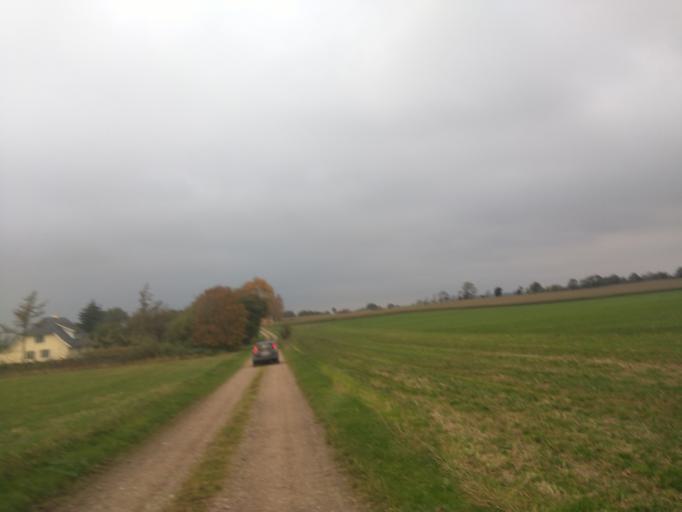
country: DK
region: Central Jutland
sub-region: Silkeborg Kommune
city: Silkeborg
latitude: 56.2472
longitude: 9.5170
